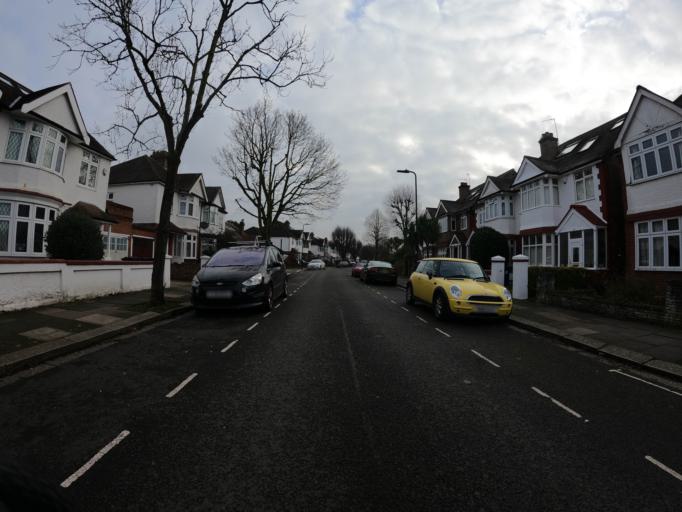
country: GB
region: England
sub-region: Greater London
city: Brentford
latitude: 51.5005
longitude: -0.3268
